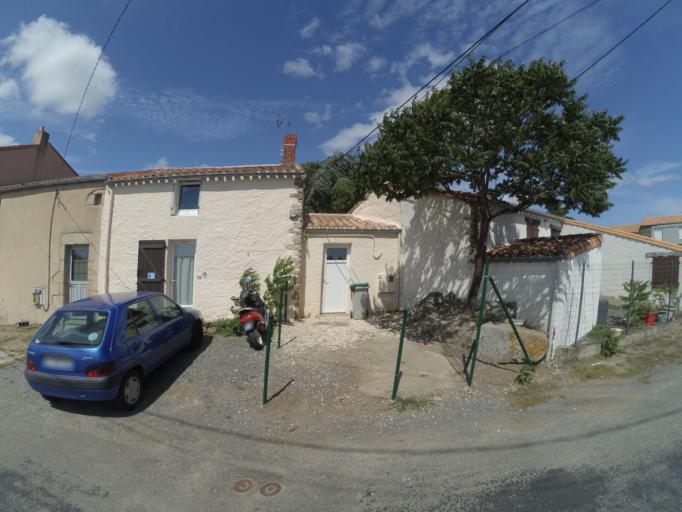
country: FR
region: Pays de la Loire
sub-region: Departement de la Loire-Atlantique
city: Saint-Hilaire-de-Clisson
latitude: 47.0734
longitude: -1.3159
